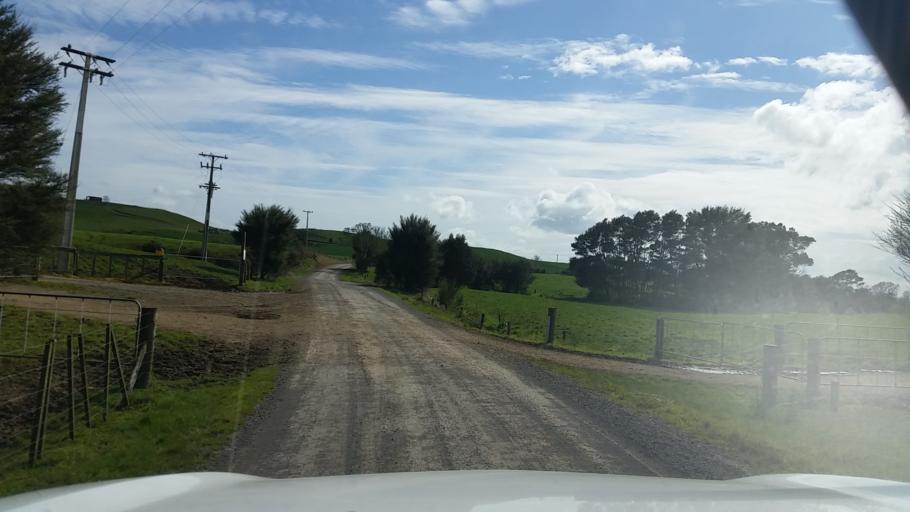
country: NZ
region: Waikato
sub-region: Hauraki District
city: Ngatea
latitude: -37.4516
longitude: 175.5002
